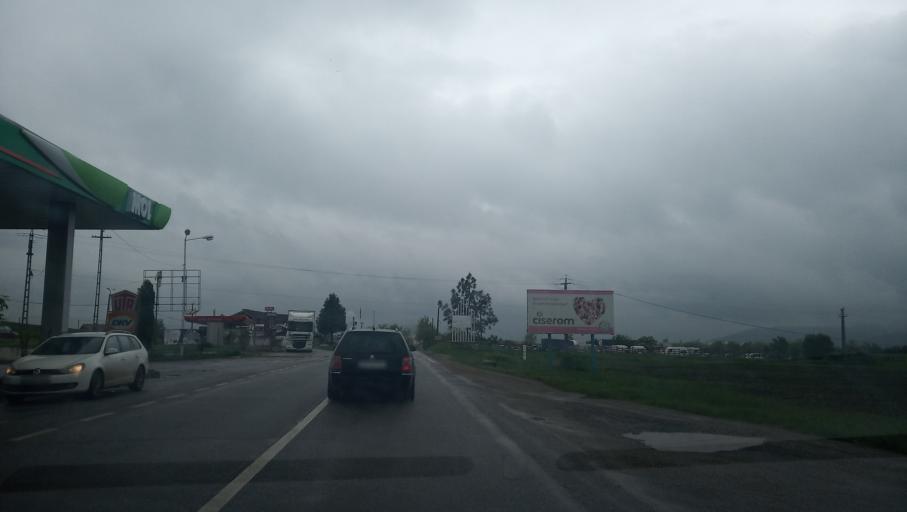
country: RO
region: Alba
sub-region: Municipiul Sebes
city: Sebes
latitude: 45.9478
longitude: 23.5861
